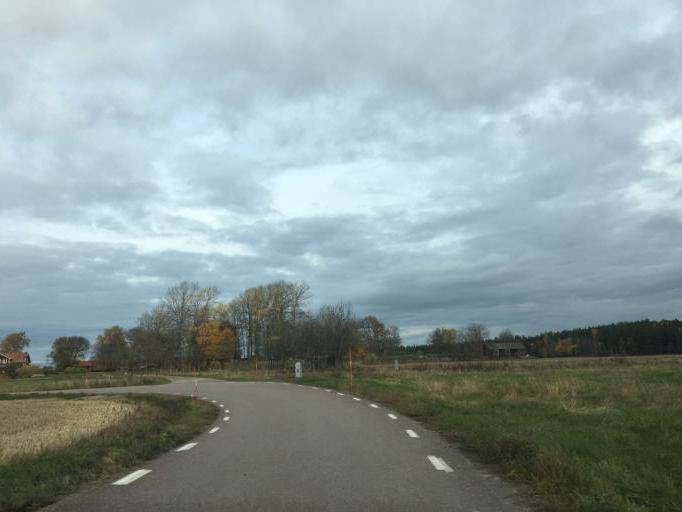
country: SE
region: Soedermanland
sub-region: Eskilstuna Kommun
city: Kvicksund
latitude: 59.5473
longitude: 16.3576
